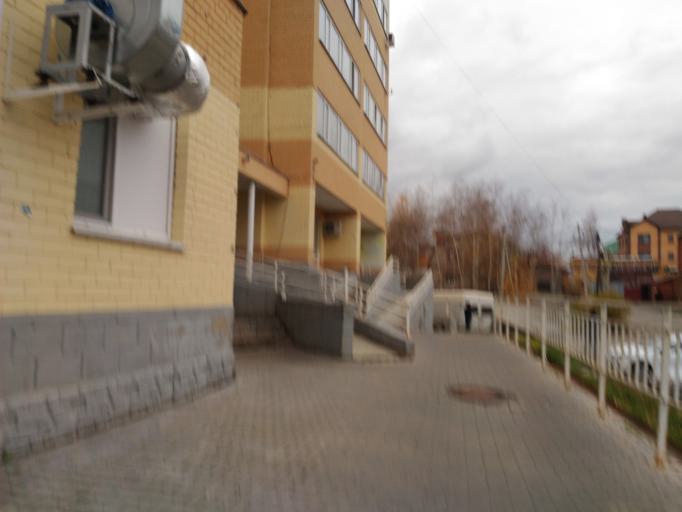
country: RU
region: Ulyanovsk
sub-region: Ulyanovskiy Rayon
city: Ulyanovsk
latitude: 54.3350
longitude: 48.3912
